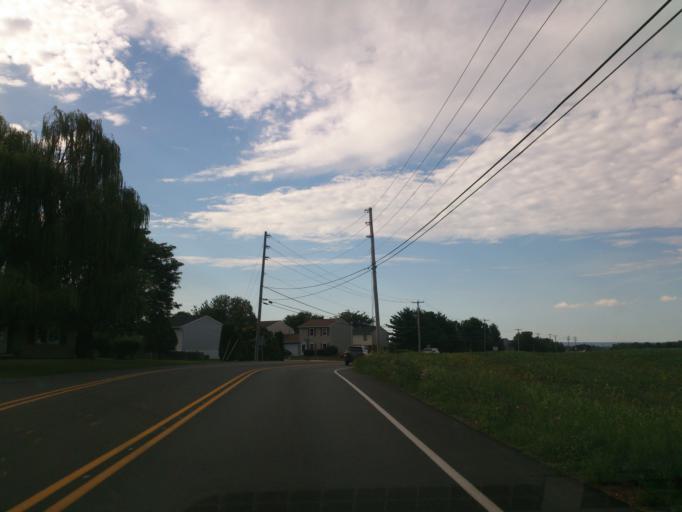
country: US
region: Pennsylvania
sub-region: Lebanon County
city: Campbelltown
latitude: 40.2794
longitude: -76.5715
